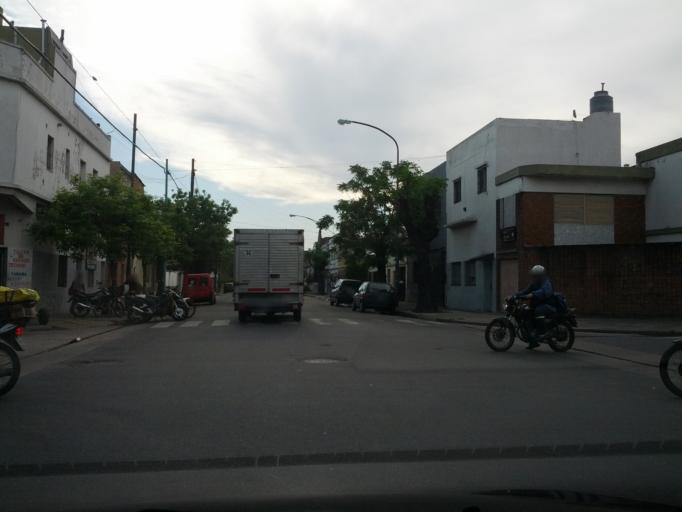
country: AR
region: Buenos Aires
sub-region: Partido de Avellaneda
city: Avellaneda
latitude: -34.6483
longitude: -58.4088
